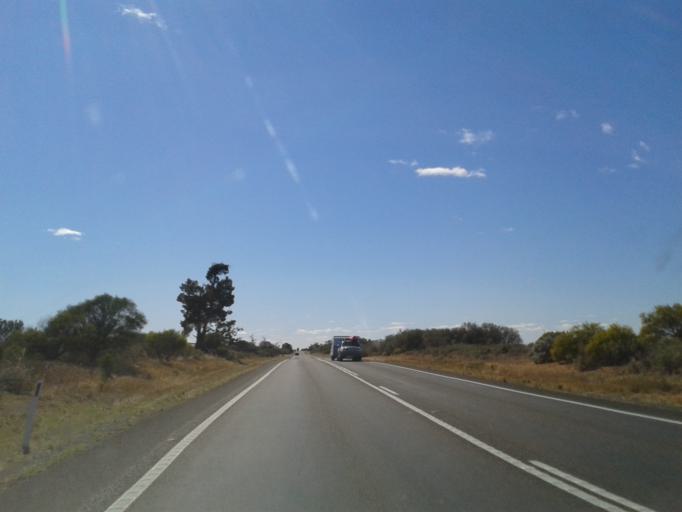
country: AU
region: New South Wales
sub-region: Wentworth
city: Dareton
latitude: -34.2761
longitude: 141.5473
